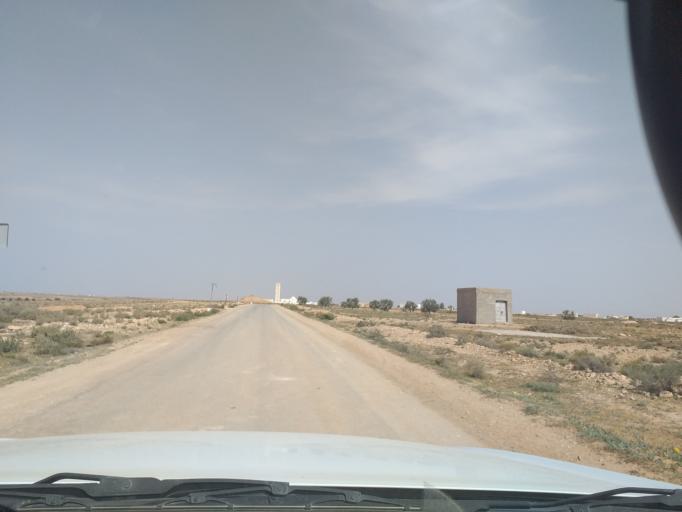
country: TN
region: Madanin
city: Medenine
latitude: 33.3127
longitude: 10.6133
